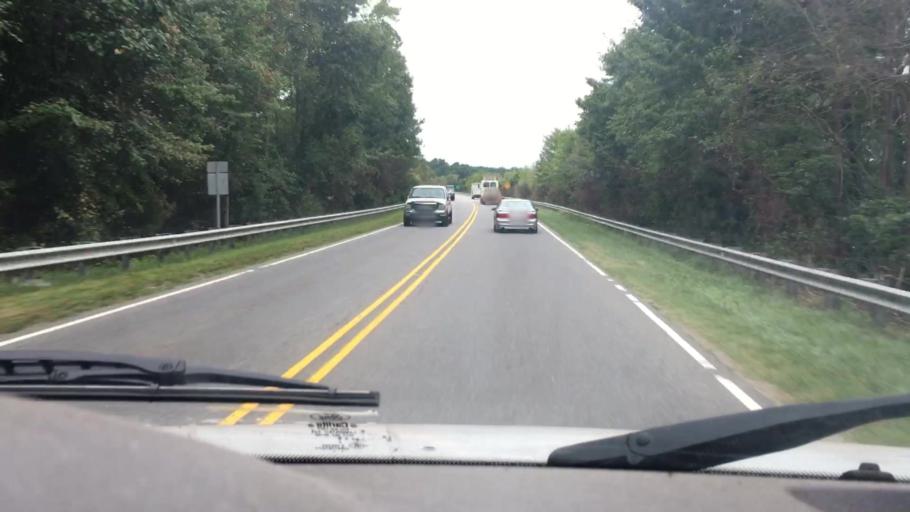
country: US
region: North Carolina
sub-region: Catawba County
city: Lake Norman of Catawba
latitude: 35.6060
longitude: -80.9381
